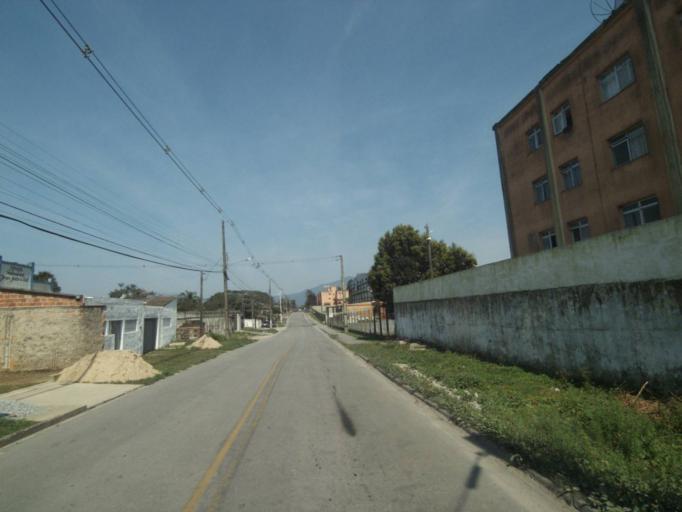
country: BR
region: Parana
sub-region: Paranagua
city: Paranagua
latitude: -25.5481
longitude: -48.5511
